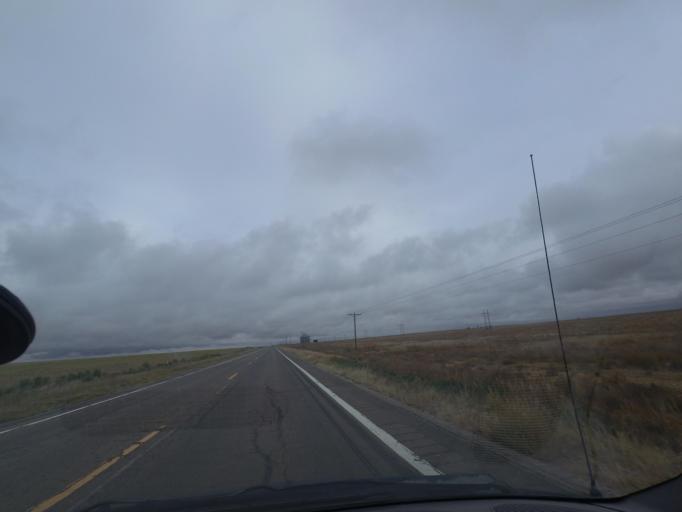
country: US
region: Colorado
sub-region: Washington County
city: Akron
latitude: 39.7412
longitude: -103.1948
